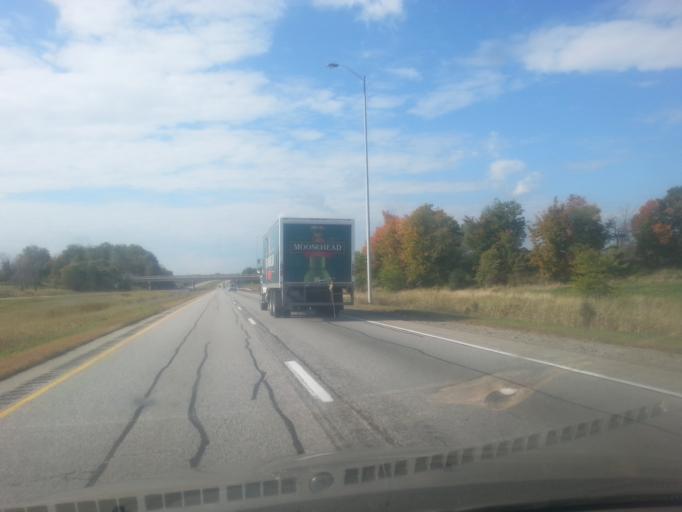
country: CA
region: Ontario
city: Gananoque
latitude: 44.3563
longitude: -76.0925
